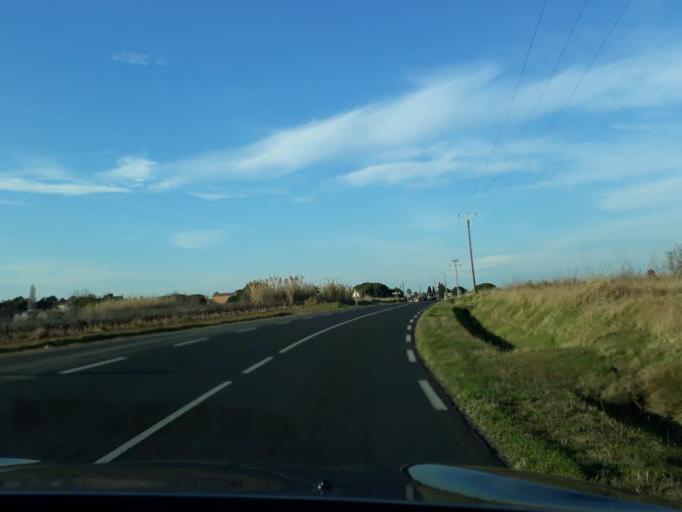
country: FR
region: Languedoc-Roussillon
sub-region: Departement de l'Herault
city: Marseillan
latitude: 43.3305
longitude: 3.5253
